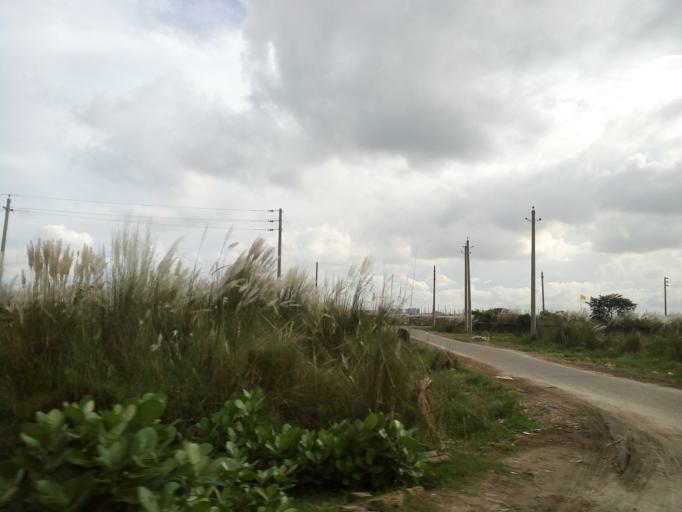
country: BD
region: Dhaka
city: Tungi
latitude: 23.8674
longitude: 90.3707
